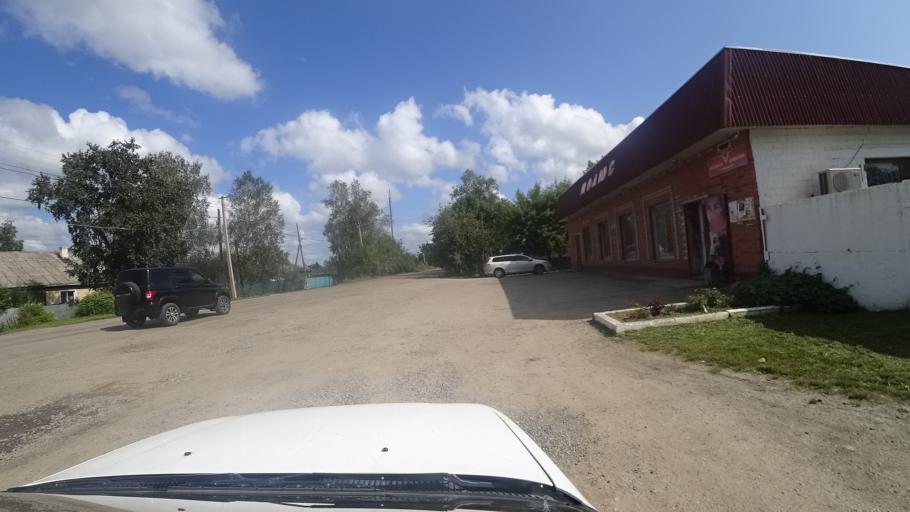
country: RU
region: Primorskiy
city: Dal'nerechensk
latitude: 45.9274
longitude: 133.7665
